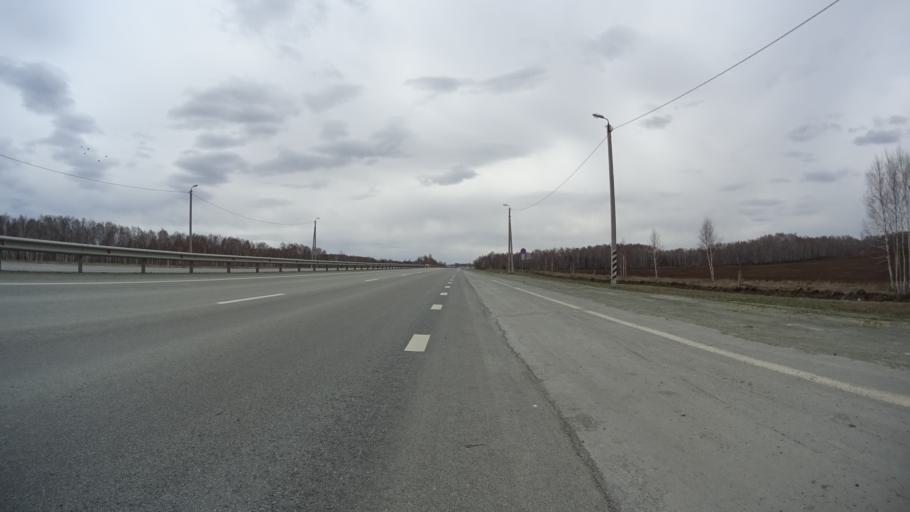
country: RU
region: Chelyabinsk
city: Yemanzhelinka
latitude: 54.8319
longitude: 61.3118
